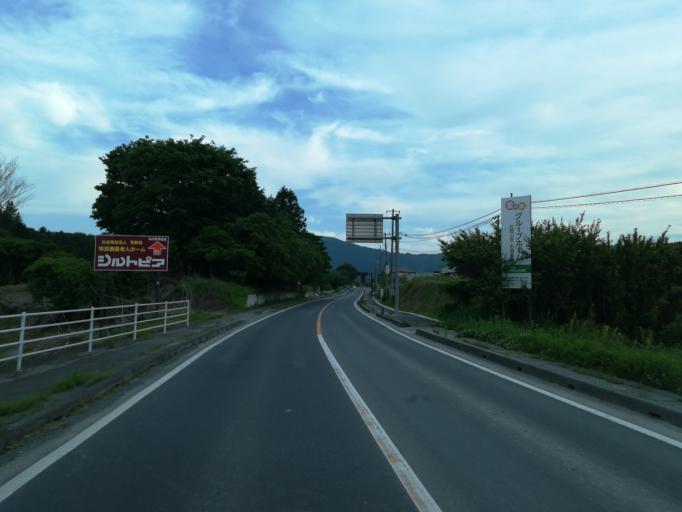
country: JP
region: Ibaraki
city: Tsukuba
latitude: 36.2058
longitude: 140.1793
